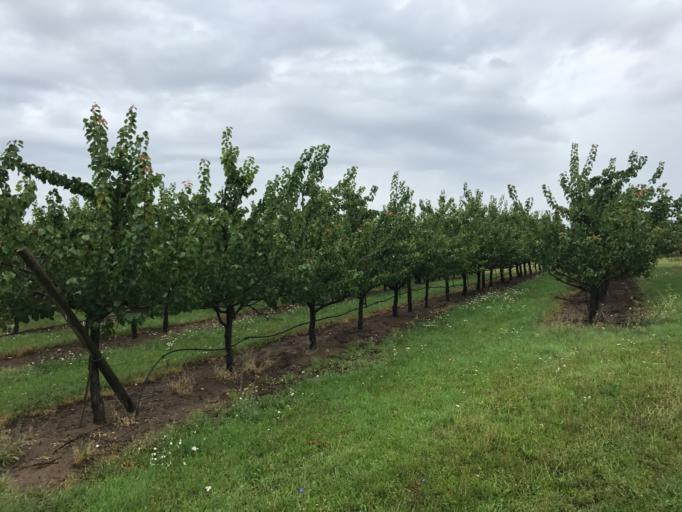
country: DE
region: Rheinland-Pfalz
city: Wackernheim
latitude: 49.9935
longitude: 8.1416
